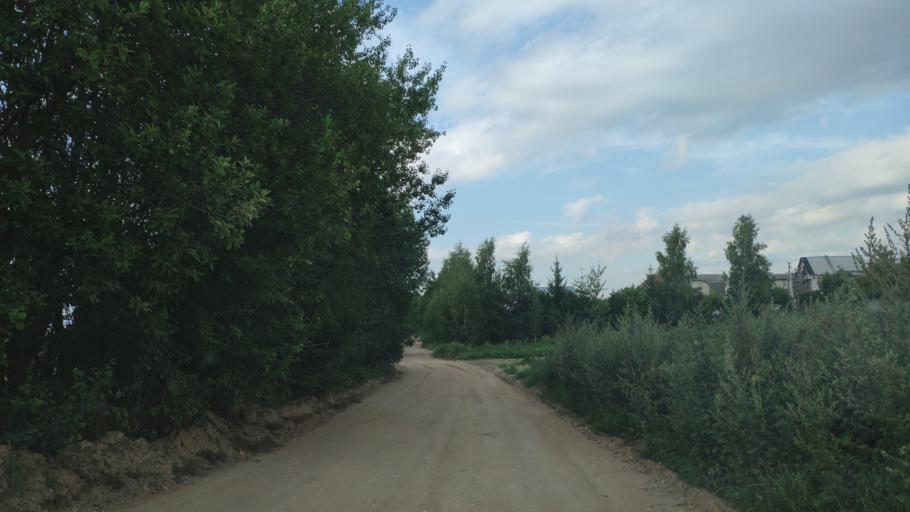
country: BY
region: Minsk
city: Khatsyezhyna
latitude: 53.8494
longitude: 27.2878
